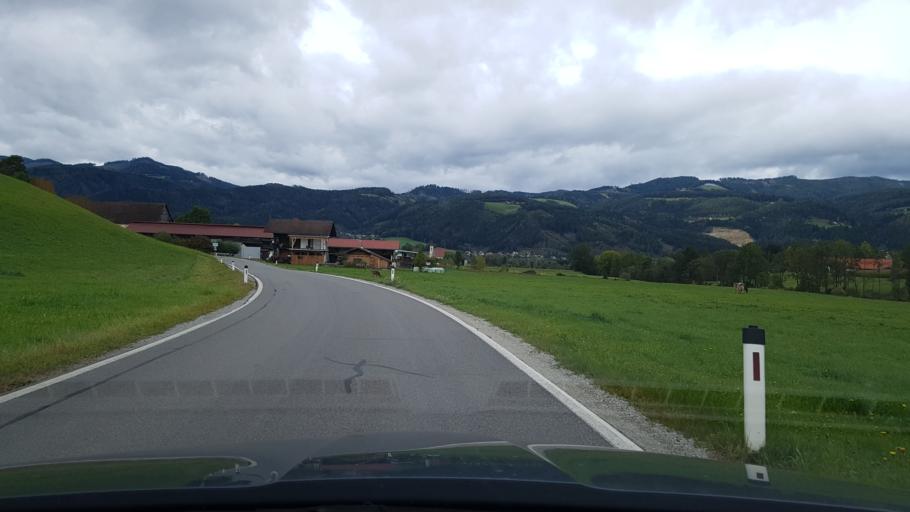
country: AT
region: Styria
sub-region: Politischer Bezirk Bruck-Muerzzuschlag
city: Allerheiligen im Muerztal
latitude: 47.4742
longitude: 15.4143
